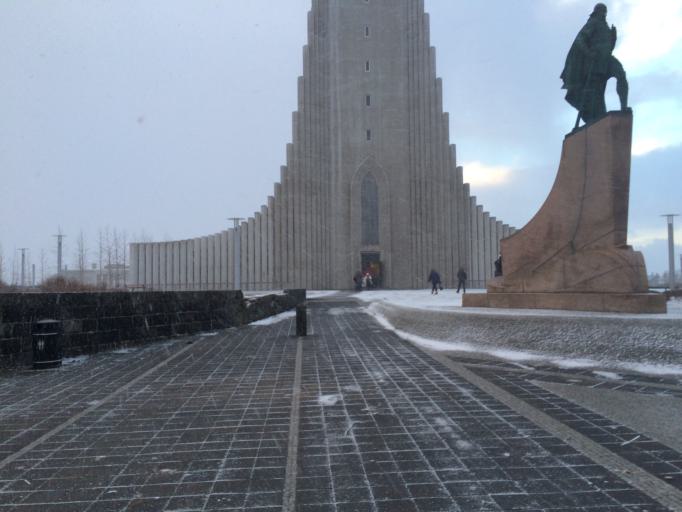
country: IS
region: Capital Region
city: Reykjavik
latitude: 64.1425
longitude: -21.9277
